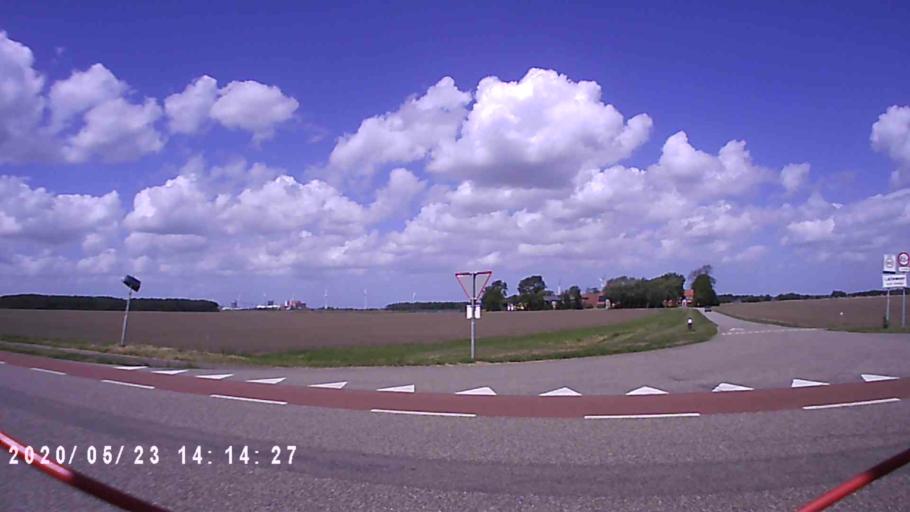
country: NL
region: Groningen
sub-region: Gemeente Delfzijl
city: Delfzijl
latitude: 53.2864
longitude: 7.0068
